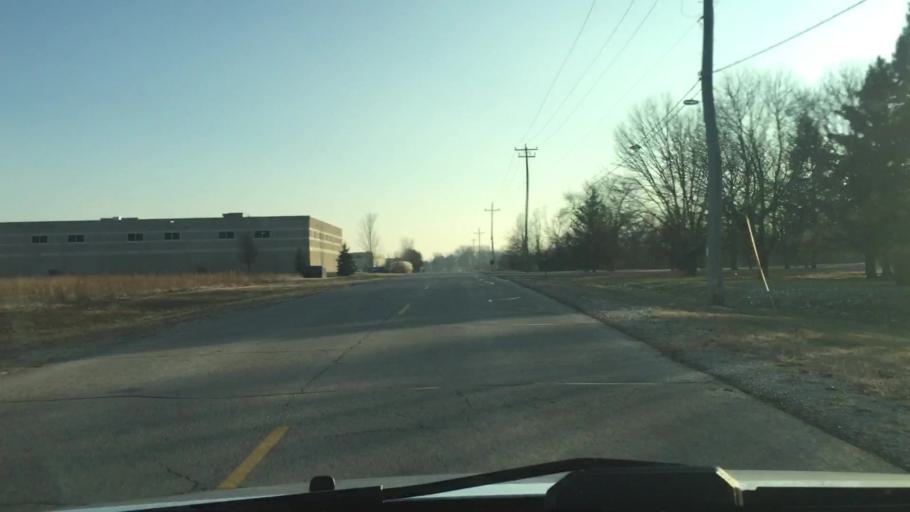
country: US
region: Wisconsin
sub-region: Waukesha County
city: Oconomowoc
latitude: 43.0678
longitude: -88.4812
